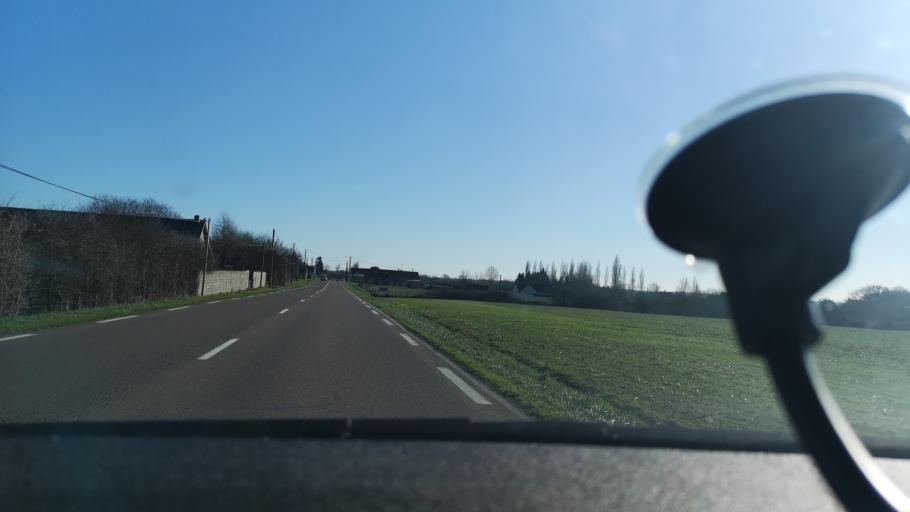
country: FR
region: Bourgogne
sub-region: Departement de Saone-et-Loire
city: Ouroux-sur-Saone
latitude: 46.7640
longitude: 4.9871
